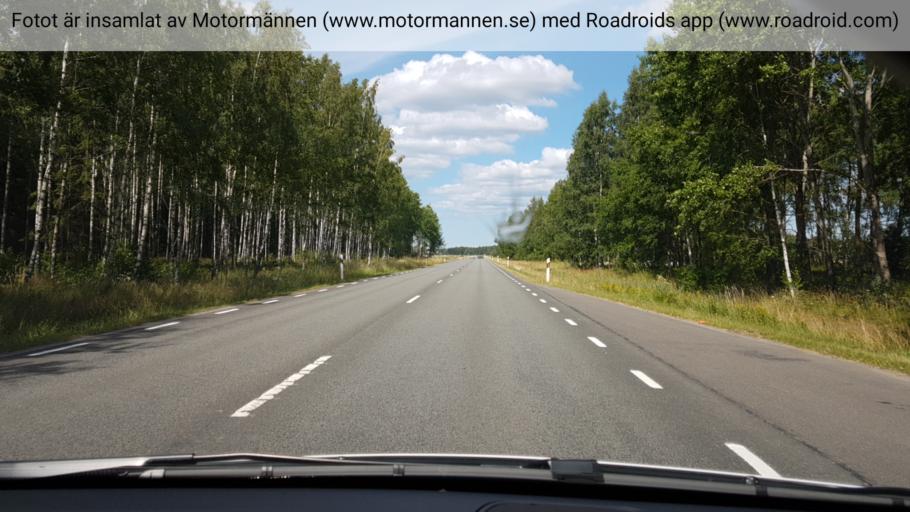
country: SE
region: Vaestra Goetaland
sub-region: Mariestads Kommun
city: Mariestad
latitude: 58.6333
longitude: 13.9197
